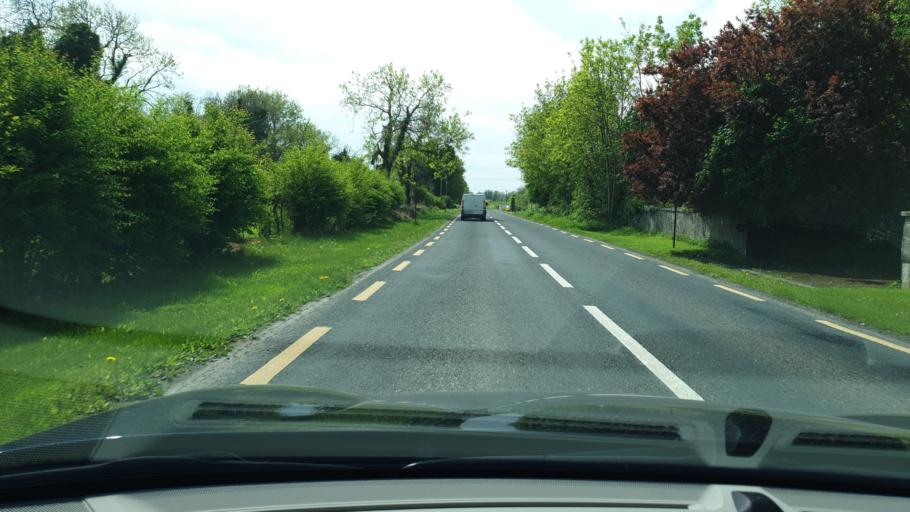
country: IE
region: Leinster
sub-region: An Mhi
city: Navan
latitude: 53.7680
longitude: -6.7254
